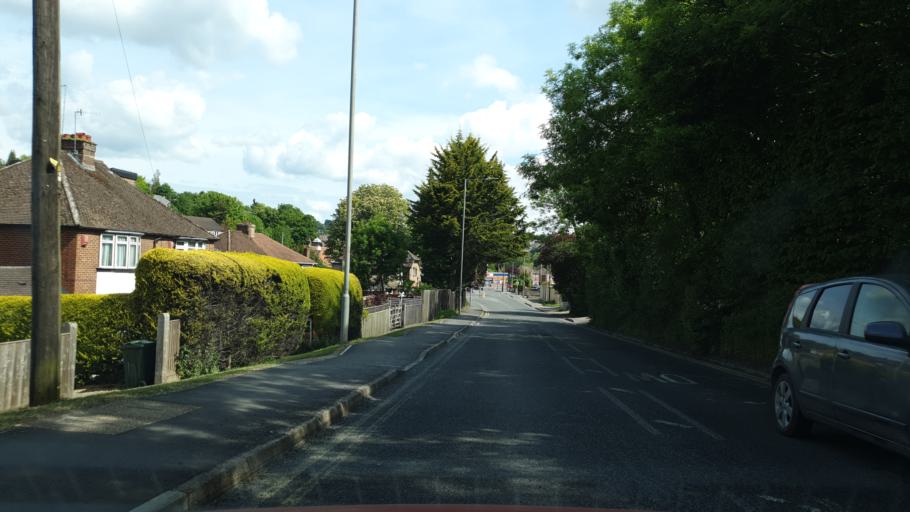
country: GB
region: England
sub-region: Buckinghamshire
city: High Wycombe
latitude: 51.6312
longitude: -0.7852
